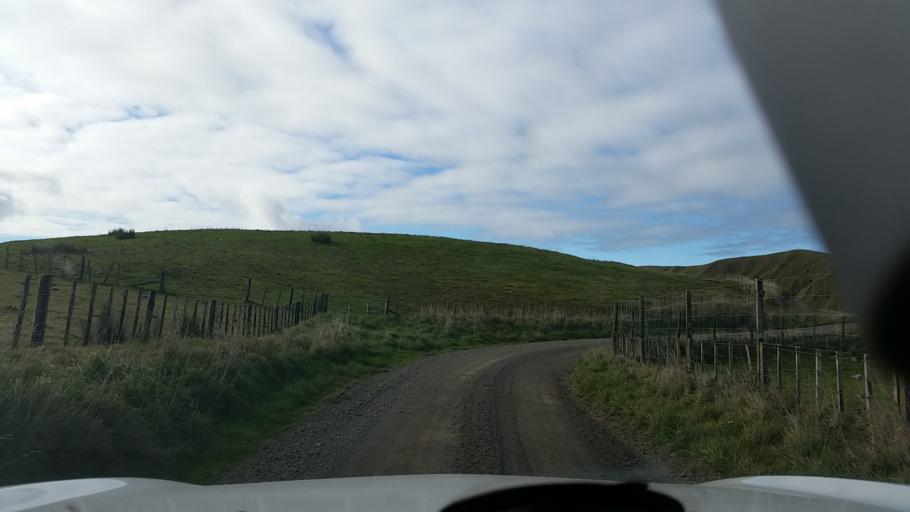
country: NZ
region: Hawke's Bay
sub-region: Napier City
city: Napier
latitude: -39.1243
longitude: 176.9159
